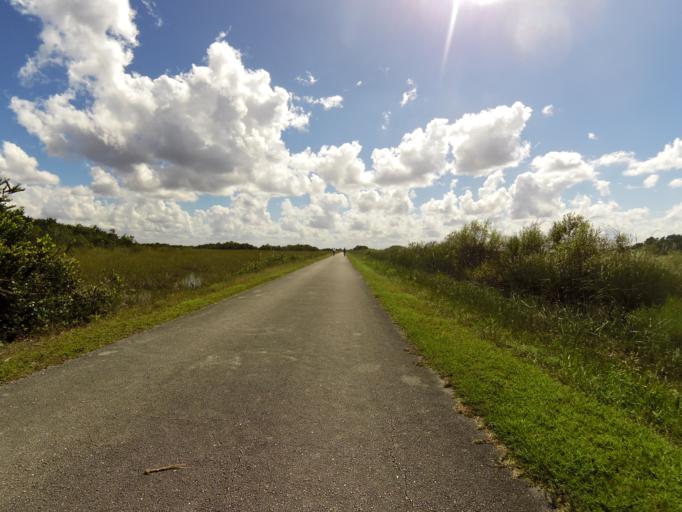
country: US
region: Florida
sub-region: Miami-Dade County
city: The Hammocks
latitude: 25.7032
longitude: -80.7668
